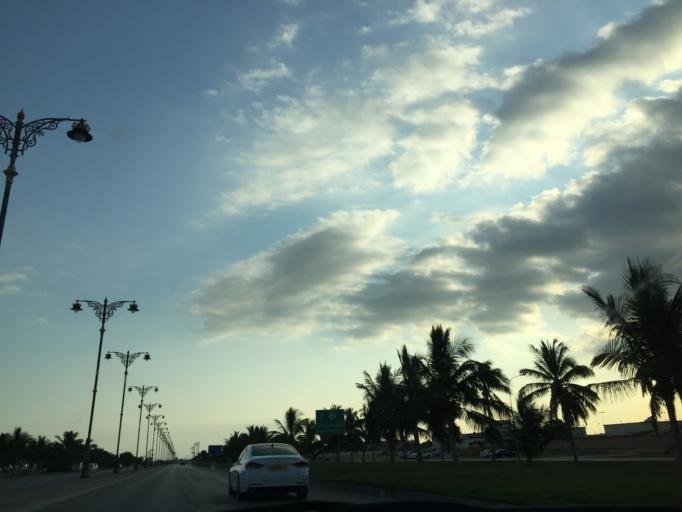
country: OM
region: Zufar
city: Salalah
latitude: 17.0431
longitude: 54.0615
